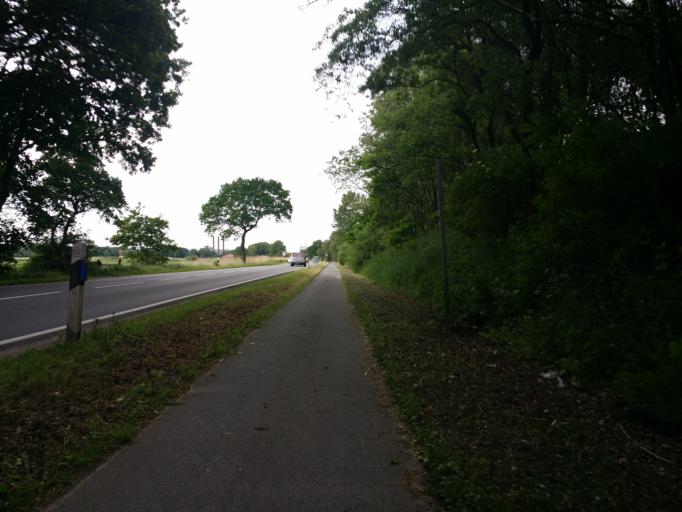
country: DE
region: Lower Saxony
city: Wittmund
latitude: 53.5608
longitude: 7.7842
